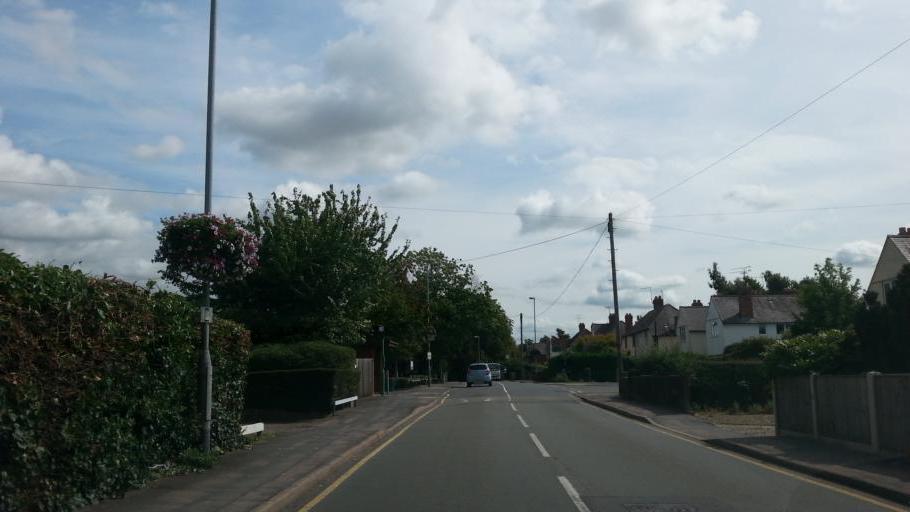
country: GB
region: England
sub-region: Leicestershire
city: Countesthorpe
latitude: 52.5537
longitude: -1.1457
